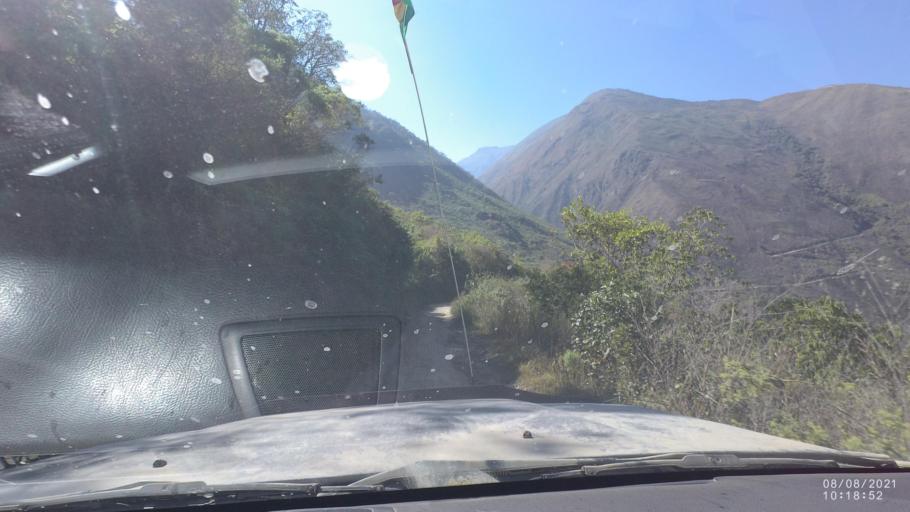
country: BO
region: La Paz
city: Quime
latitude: -16.6860
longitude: -66.7288
